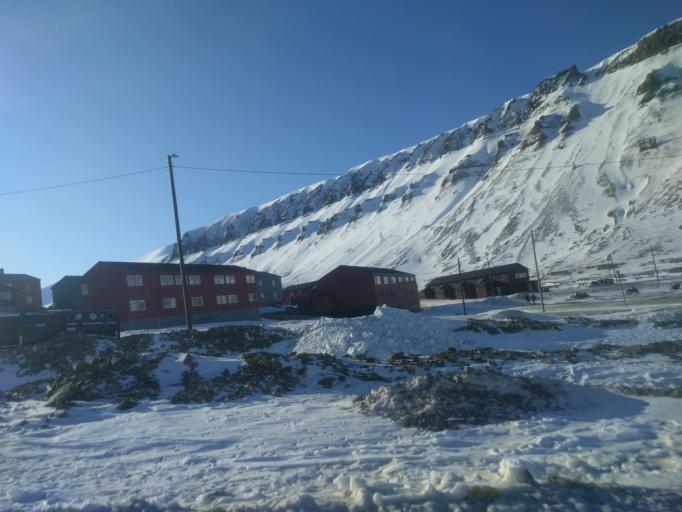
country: SJ
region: Svalbard
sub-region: Spitsbergen
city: Longyearbyen
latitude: 78.2136
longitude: 15.6263
